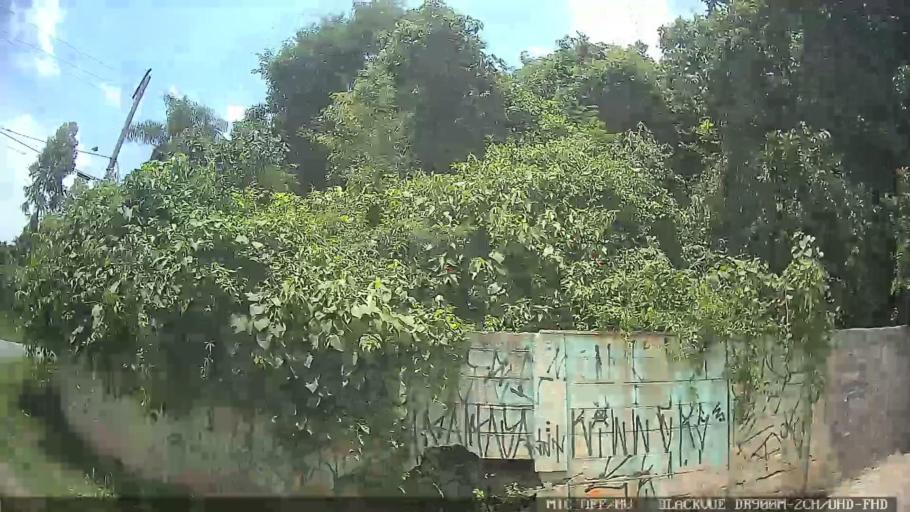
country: BR
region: Sao Paulo
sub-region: Ferraz De Vasconcelos
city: Ferraz de Vasconcelos
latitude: -23.5588
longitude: -46.3567
